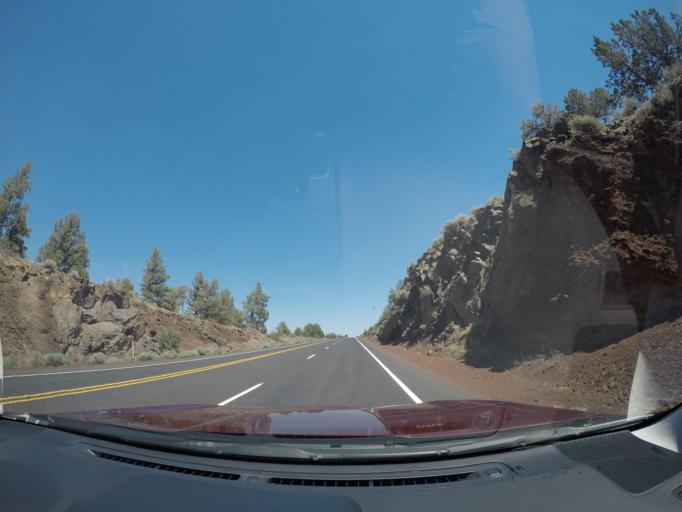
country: US
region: Oregon
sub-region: Deschutes County
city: Sisters
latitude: 44.2948
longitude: -121.3903
